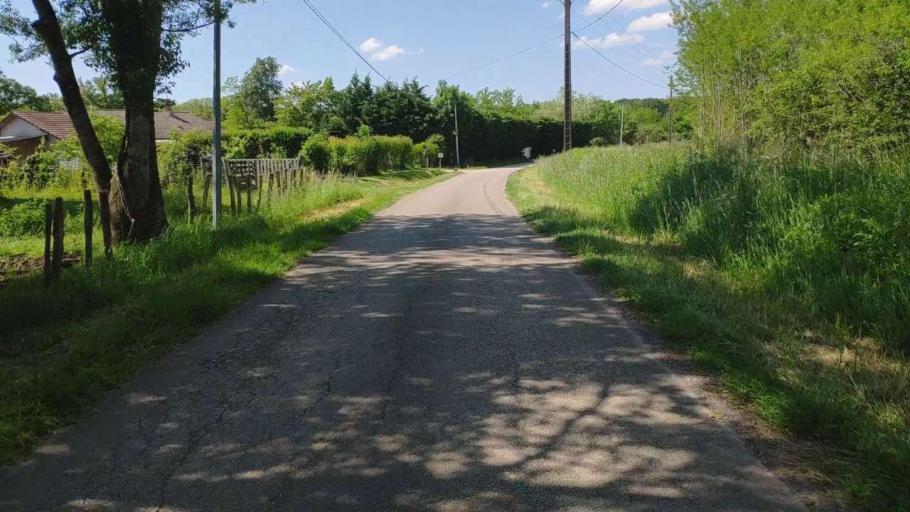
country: FR
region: Franche-Comte
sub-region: Departement du Jura
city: Bletterans
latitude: 46.8125
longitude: 5.4091
